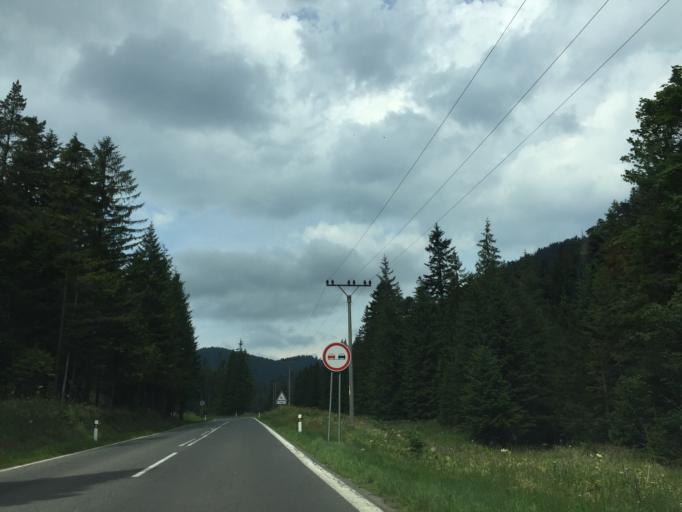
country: SK
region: Presovsky
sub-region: Okres Poprad
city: Zdiar
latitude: 49.2350
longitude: 20.3134
